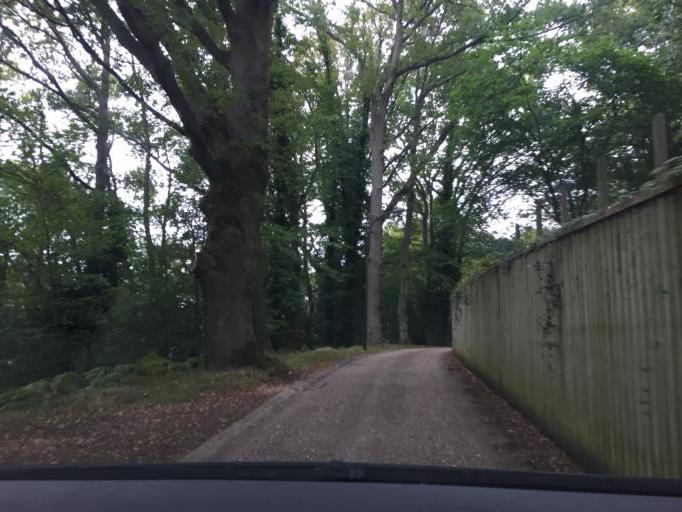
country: FR
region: Ile-de-France
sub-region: Departement de l'Essonne
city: Villiers-le-Bacle
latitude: 48.7206
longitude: 2.1242
